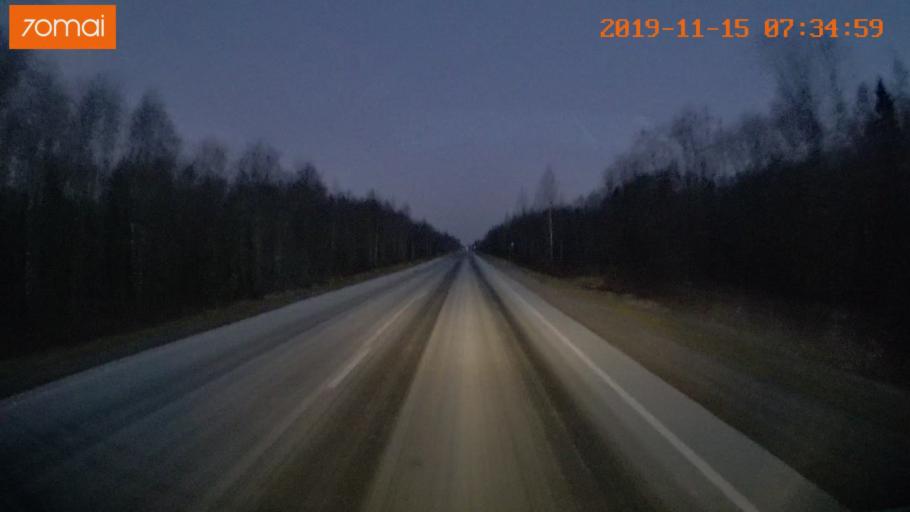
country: RU
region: Vologda
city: Sheksna
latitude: 58.7265
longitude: 38.4590
